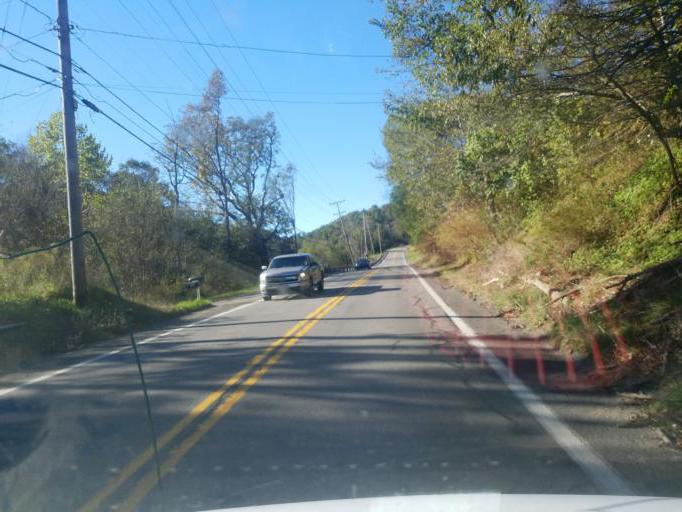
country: US
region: Pennsylvania
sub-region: Beaver County
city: Midland
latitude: 40.5435
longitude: -80.4168
